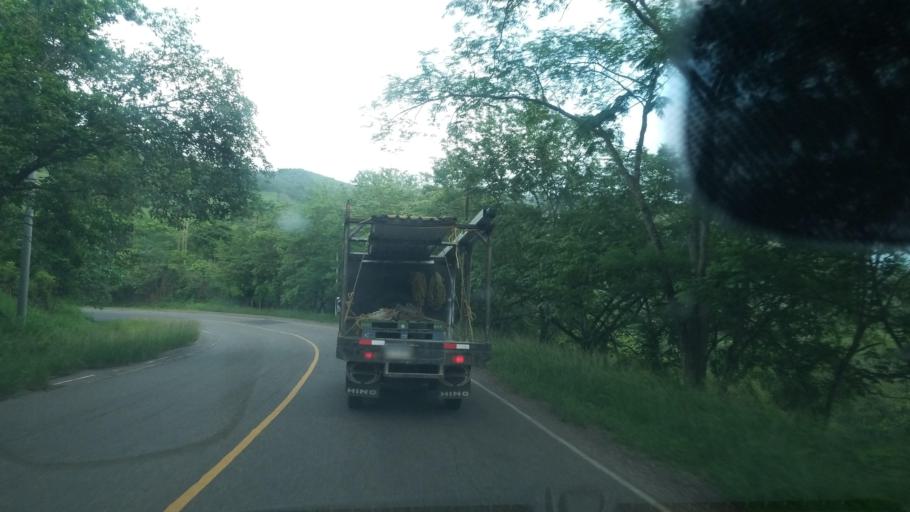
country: HN
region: Santa Barbara
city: Ceguaca
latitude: 14.8089
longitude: -88.1874
